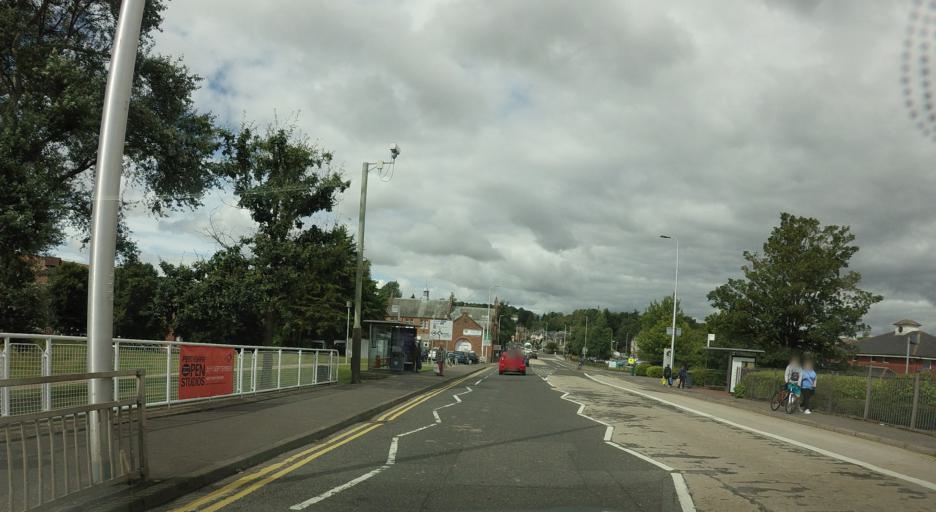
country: GB
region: Scotland
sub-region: Perth and Kinross
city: Perth
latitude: 56.3956
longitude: -3.4427
